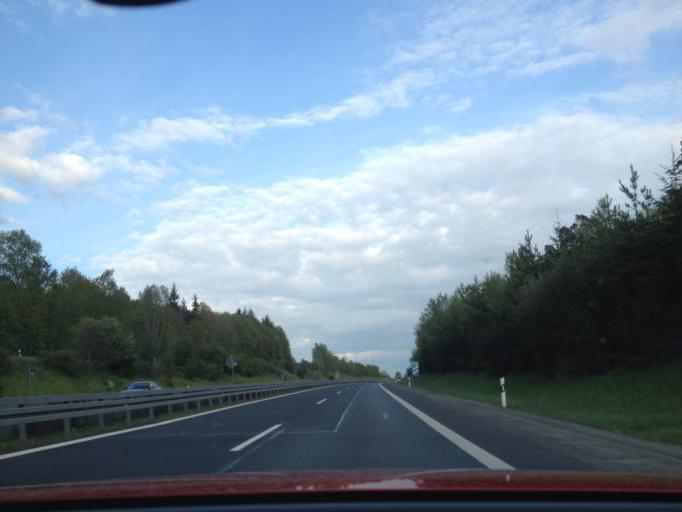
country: DE
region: Bavaria
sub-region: Upper Palatinate
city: Pechbrunn
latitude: 49.9520
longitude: 12.2027
